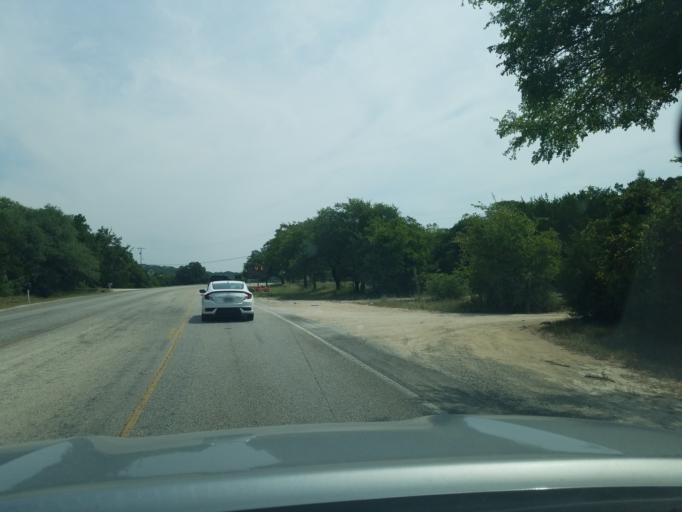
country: US
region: Texas
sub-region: Comal County
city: Bulverde
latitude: 29.7981
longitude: -98.4429
